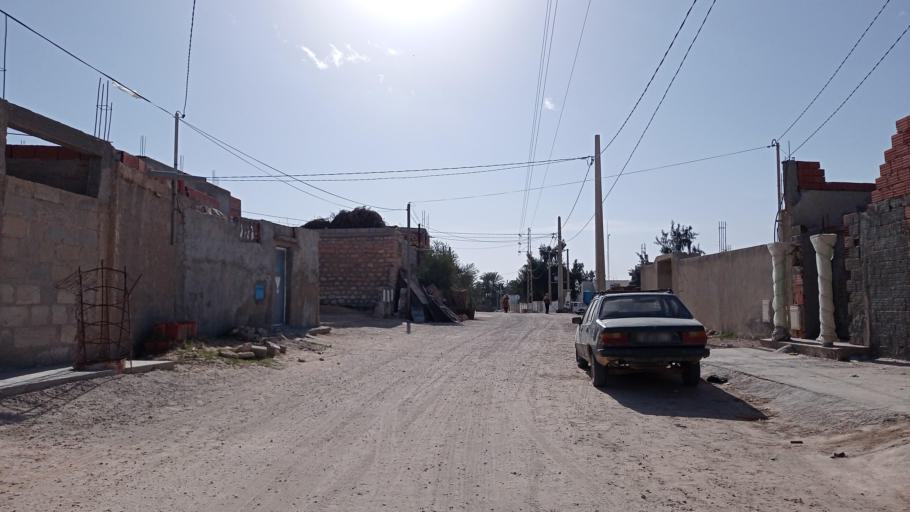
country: TN
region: Qabis
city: Gabes
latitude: 33.8317
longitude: 10.1116
